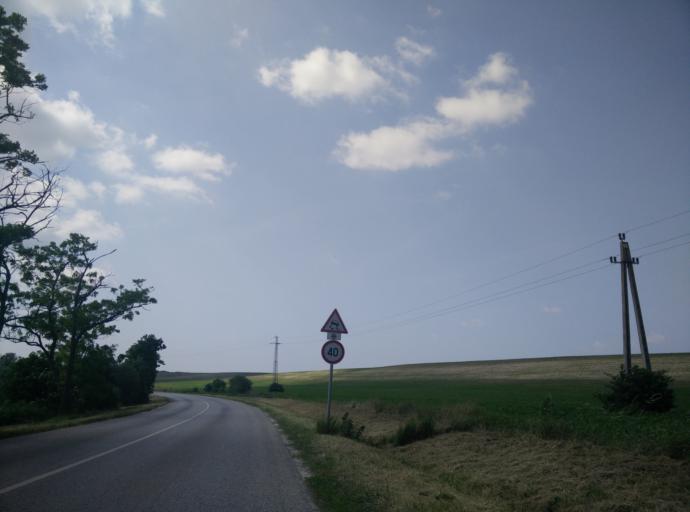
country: HU
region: Pest
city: Biatorbagy
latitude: 47.4736
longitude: 18.8010
